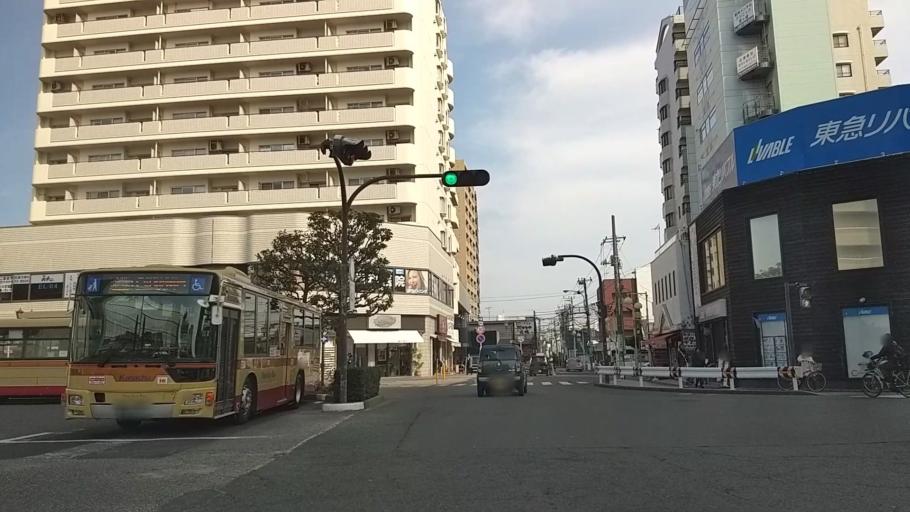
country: JP
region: Kanagawa
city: Chigasaki
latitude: 35.3299
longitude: 139.4070
